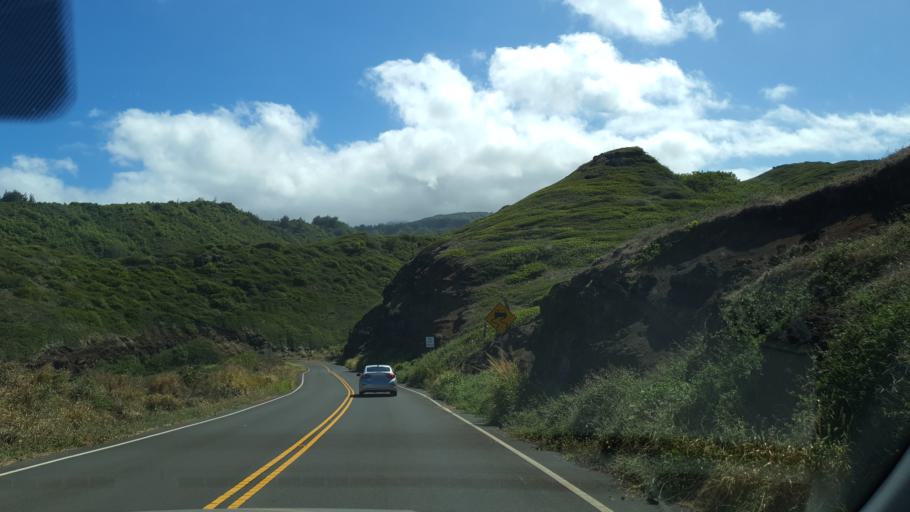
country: US
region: Hawaii
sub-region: Maui County
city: Waihee-Waiehu
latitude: 21.0122
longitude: -156.5694
